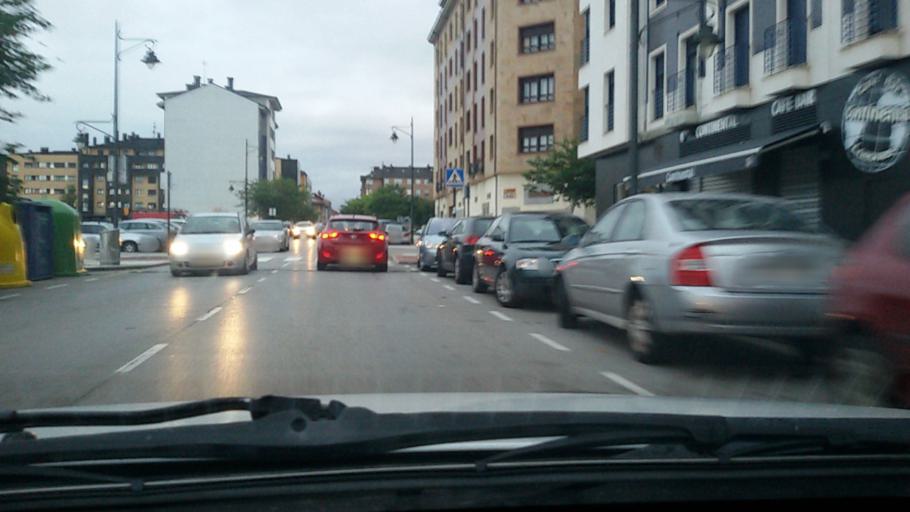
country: ES
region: Asturias
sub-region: Province of Asturias
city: Lugones
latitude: 43.4043
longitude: -5.8063
